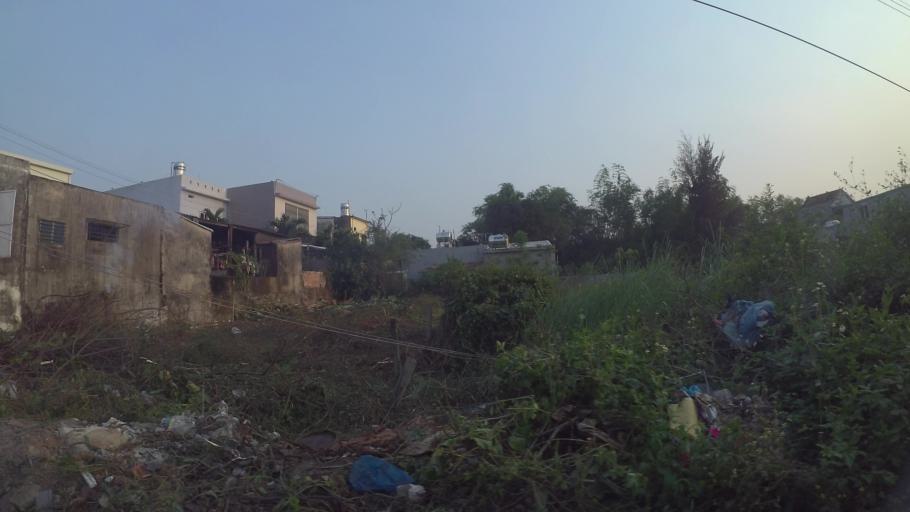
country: VN
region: Da Nang
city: Ngu Hanh Son
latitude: 15.9525
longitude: 108.2541
